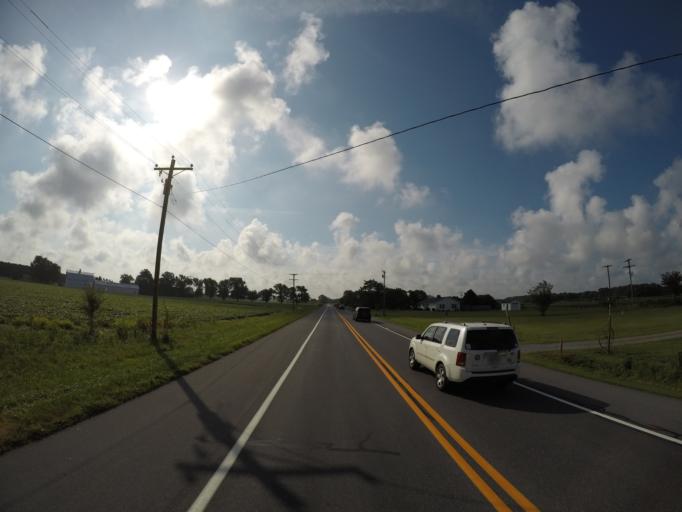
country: US
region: Delaware
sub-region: Sussex County
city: Bridgeville
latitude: 38.7603
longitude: -75.6379
